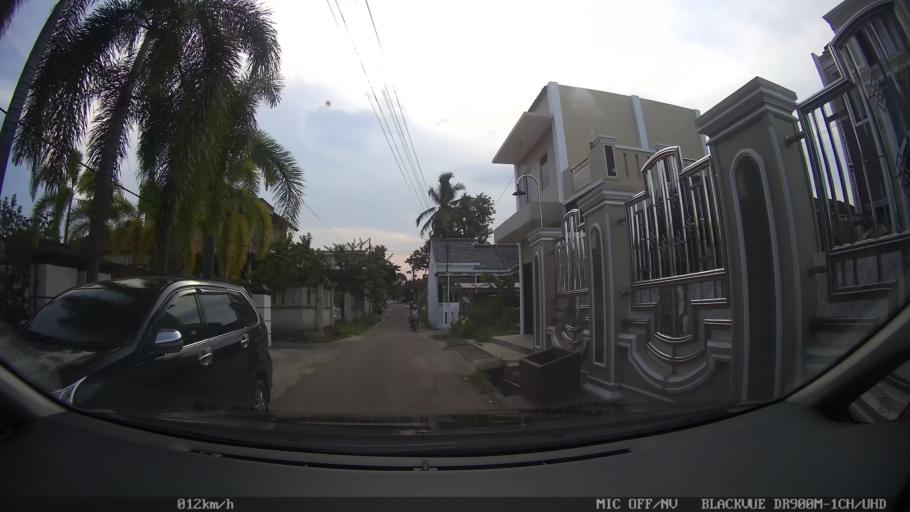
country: ID
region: Lampung
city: Kedaton
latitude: -5.3814
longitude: 105.2328
